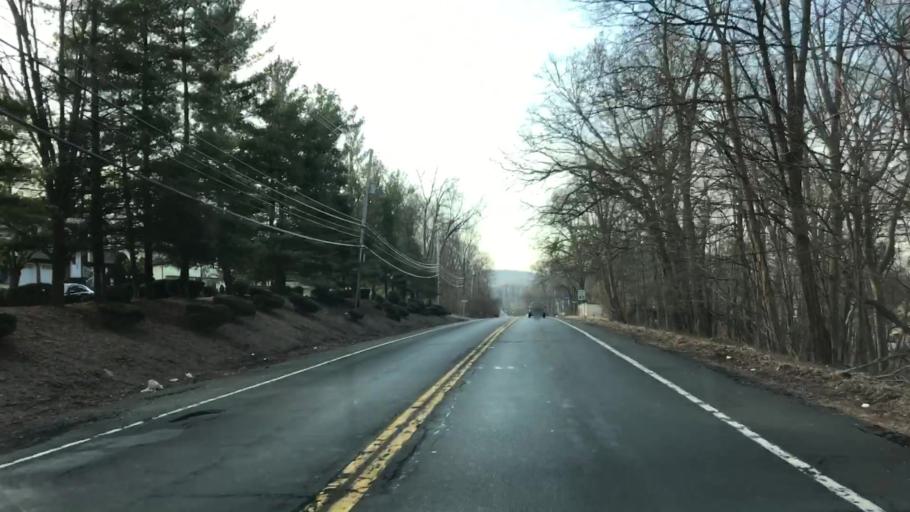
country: US
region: New York
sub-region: Rockland County
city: Congers
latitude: 41.1333
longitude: -73.9392
